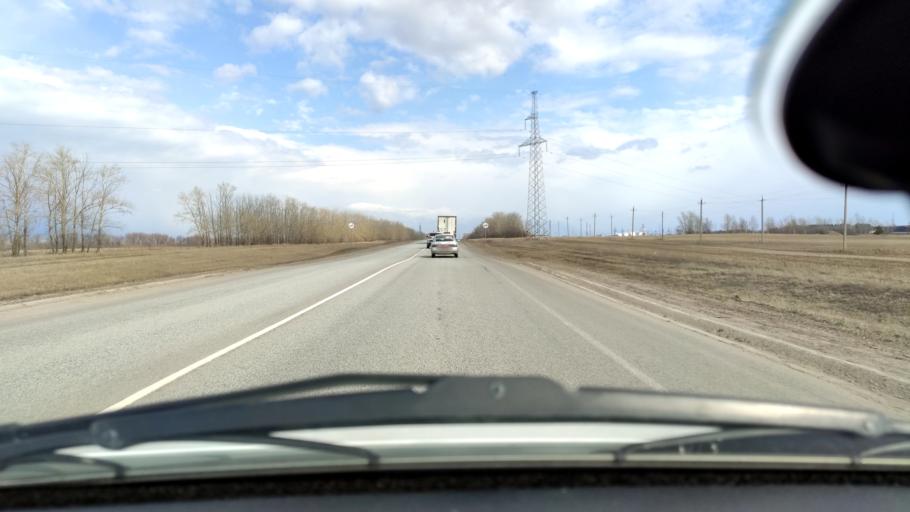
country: RU
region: Bashkortostan
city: Buzdyak
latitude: 54.6708
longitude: 54.7533
